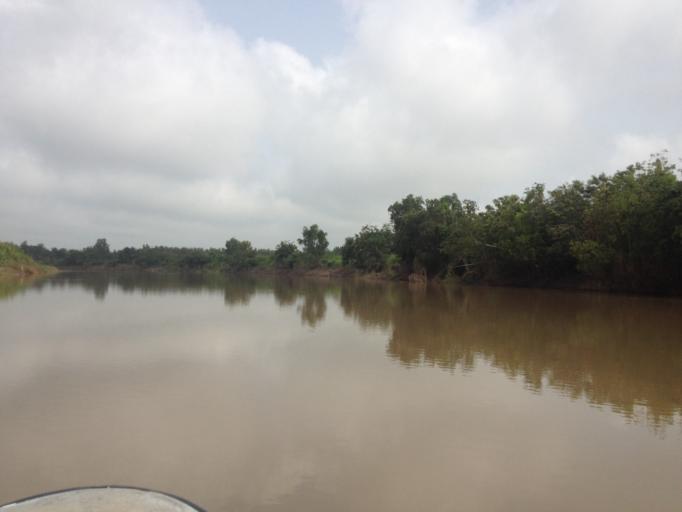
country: BJ
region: Mono
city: Come
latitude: 6.3914
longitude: 1.7734
